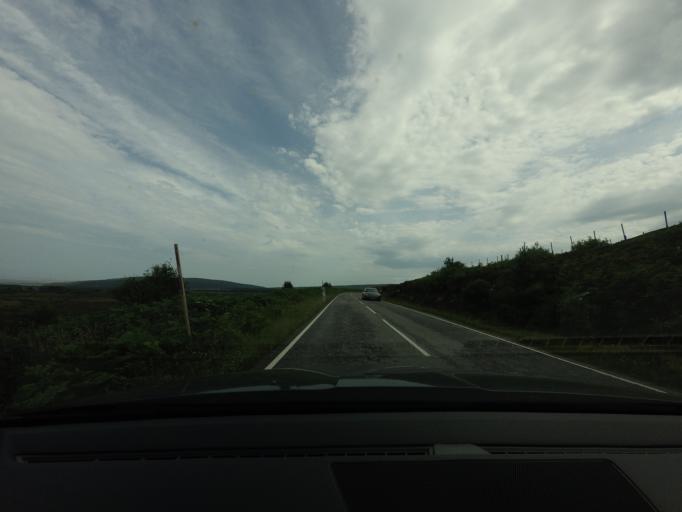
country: GB
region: Scotland
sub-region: Highland
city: Alness
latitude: 57.8225
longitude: -4.2591
